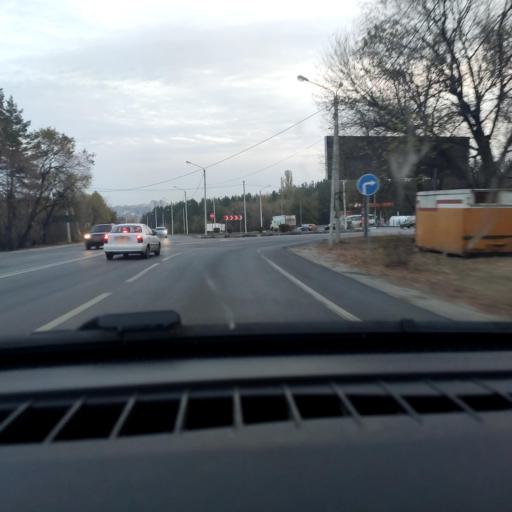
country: RU
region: Voronezj
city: Pridonskoy
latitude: 51.6761
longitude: 39.1152
